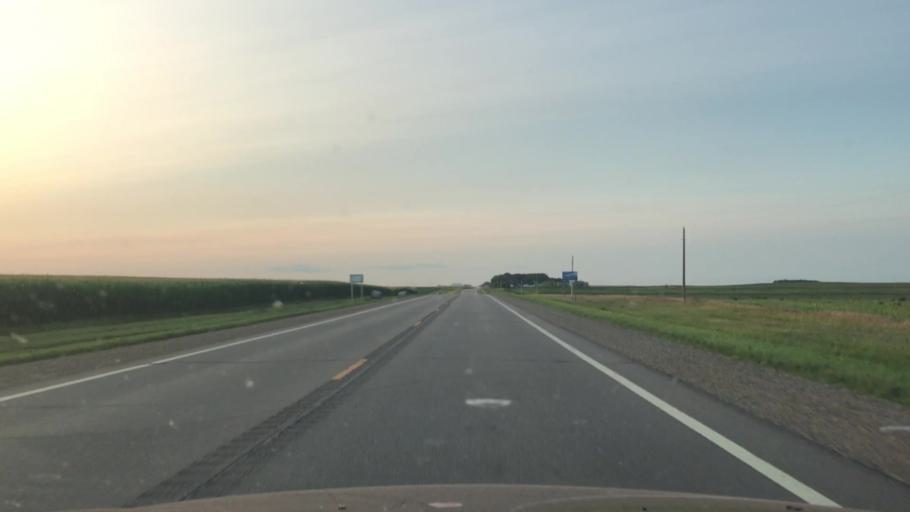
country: US
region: Minnesota
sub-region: Redwood County
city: Redwood Falls
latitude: 44.4353
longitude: -95.1176
